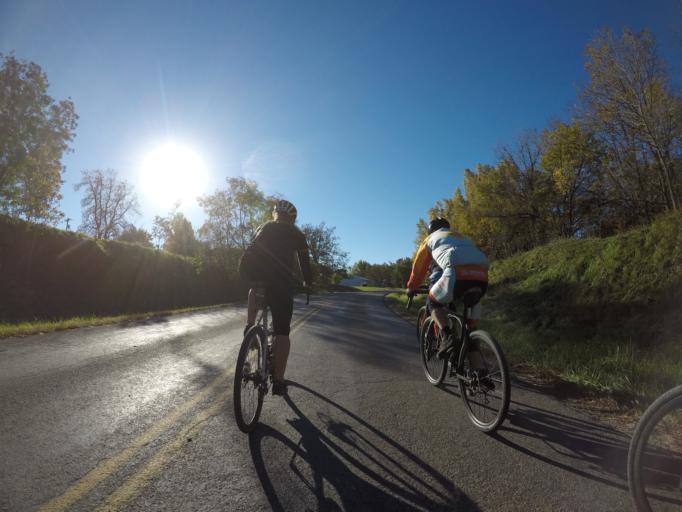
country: US
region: Kansas
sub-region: Morris County
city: Council Grove
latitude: 38.8691
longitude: -96.4886
